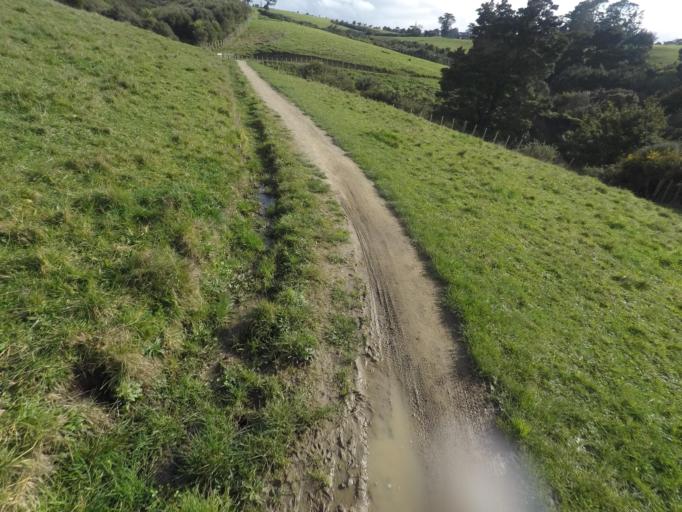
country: NZ
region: Auckland
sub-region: Auckland
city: Manukau City
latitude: -36.9945
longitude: 174.9101
